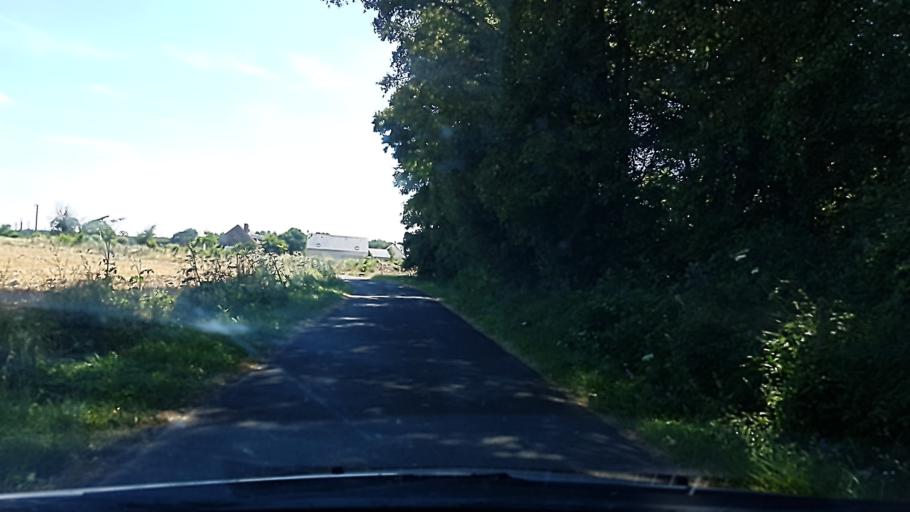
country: FR
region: Pays de la Loire
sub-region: Departement de Maine-et-Loire
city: Corze
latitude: 47.5314
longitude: -0.3868
